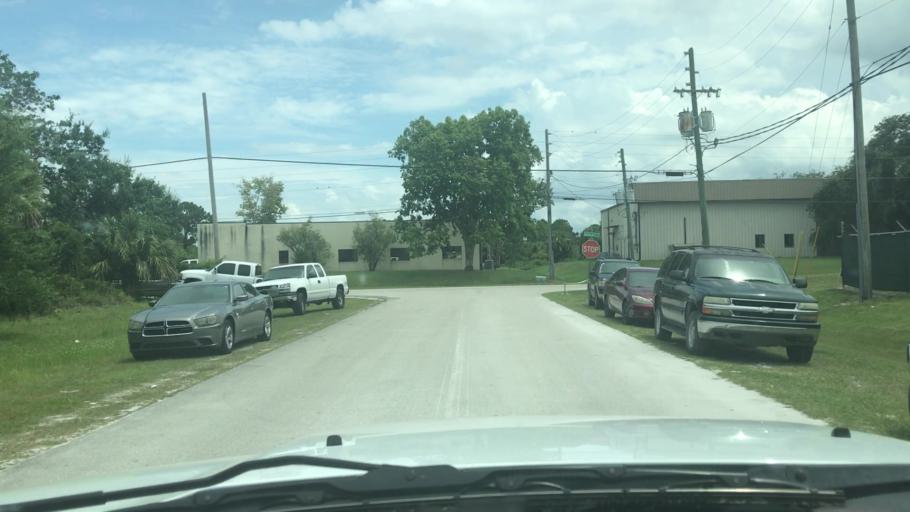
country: US
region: Florida
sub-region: Saint Lucie County
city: Fort Pierce North
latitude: 27.4888
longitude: -80.3538
